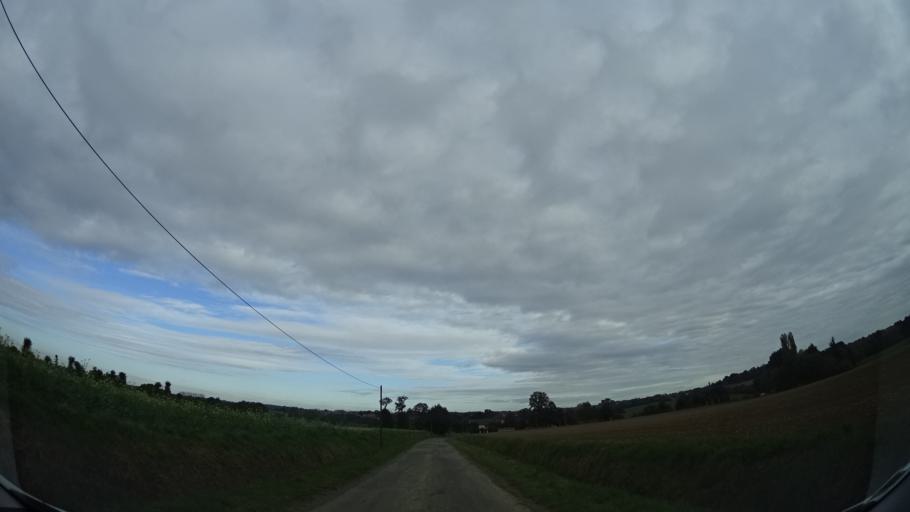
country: FR
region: Brittany
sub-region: Departement d'Ille-et-Vilaine
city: Vignoc
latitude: 48.2369
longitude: -1.7792
